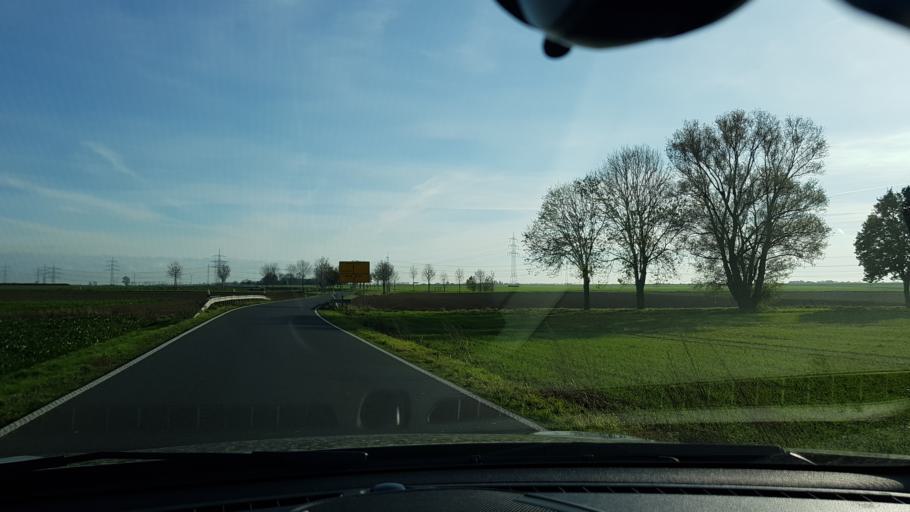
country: DE
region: North Rhine-Westphalia
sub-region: Regierungsbezirk Dusseldorf
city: Neubrueck
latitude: 51.0910
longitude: 6.6499
